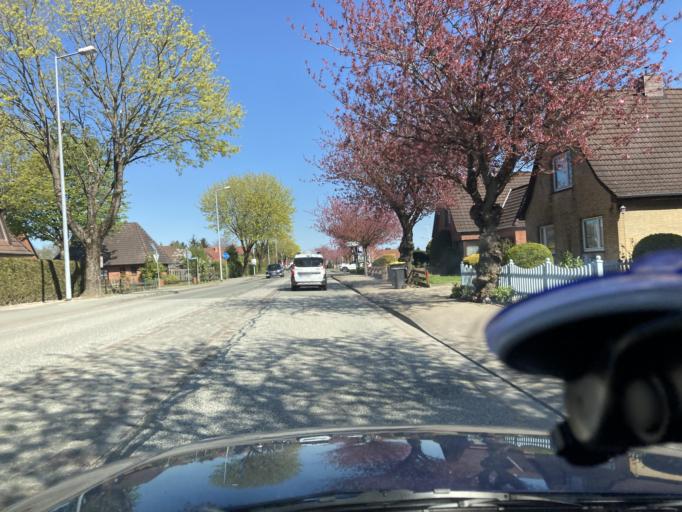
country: DE
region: Schleswig-Holstein
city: Heide
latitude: 54.1821
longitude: 9.0903
